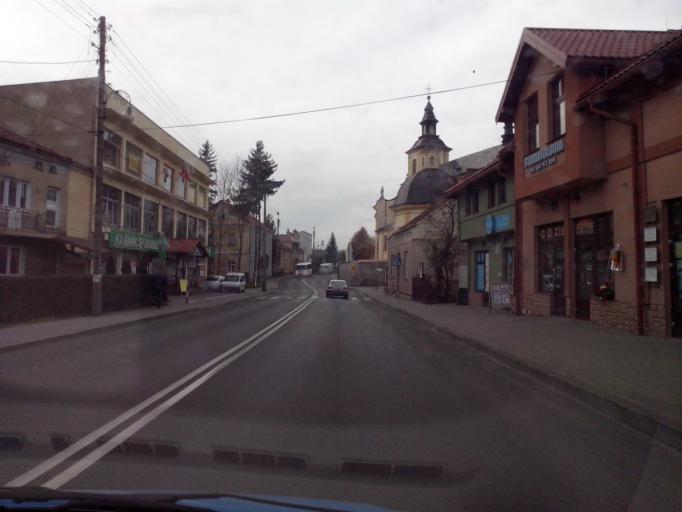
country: PL
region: Subcarpathian Voivodeship
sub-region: Powiat strzyzowski
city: Czudec
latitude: 49.9455
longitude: 21.8374
